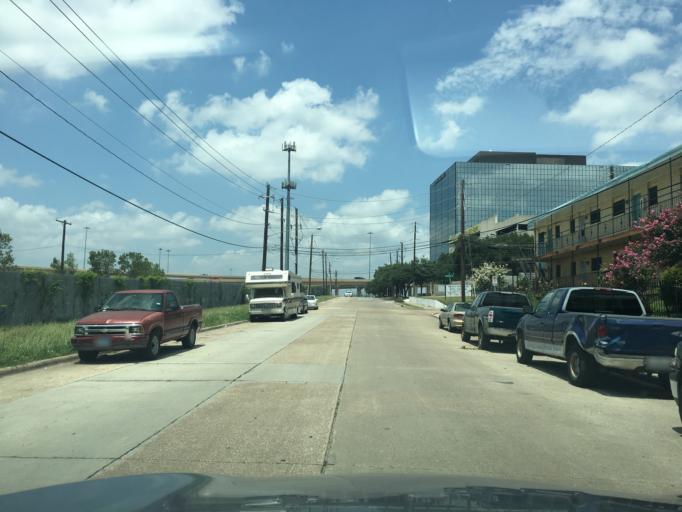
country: US
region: Texas
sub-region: Dallas County
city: Richardson
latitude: 32.9211
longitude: -96.7608
